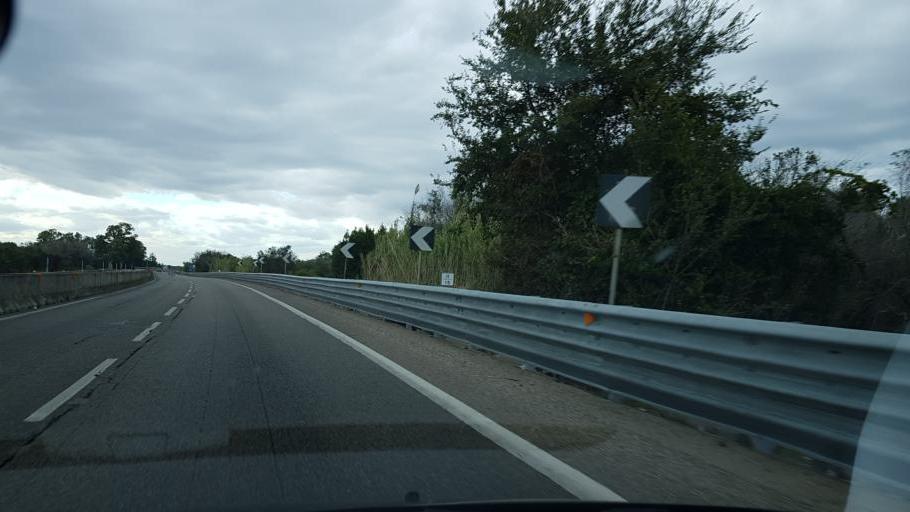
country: IT
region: Apulia
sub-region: Provincia di Brindisi
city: Torchiarolo
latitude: 40.5010
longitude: 18.0309
